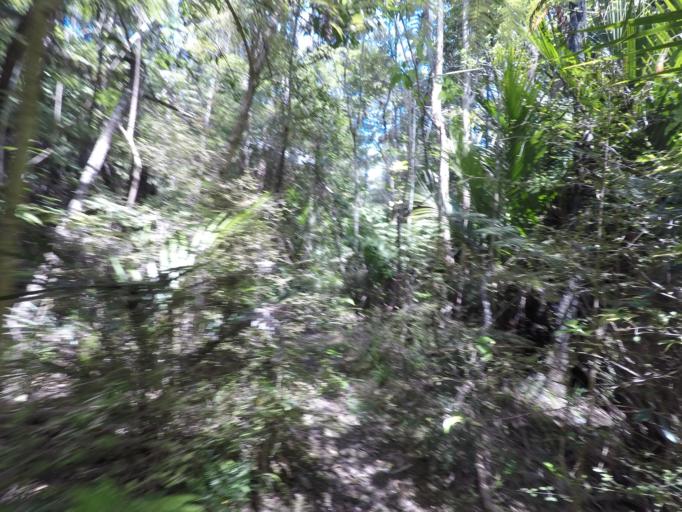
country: NZ
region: Auckland
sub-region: Auckland
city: Titirangi
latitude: -36.9738
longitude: 174.6308
